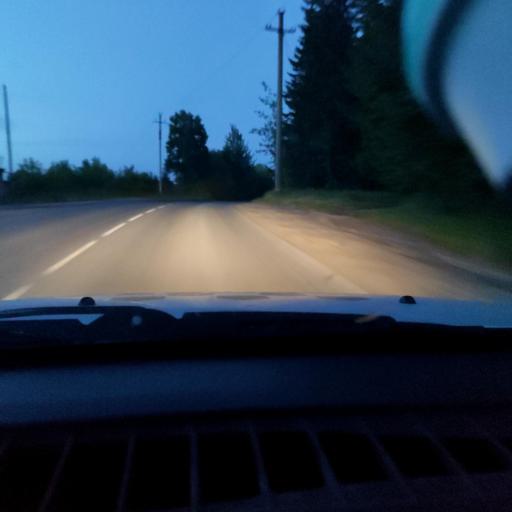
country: RU
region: Perm
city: Polazna
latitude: 58.2907
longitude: 56.4042
